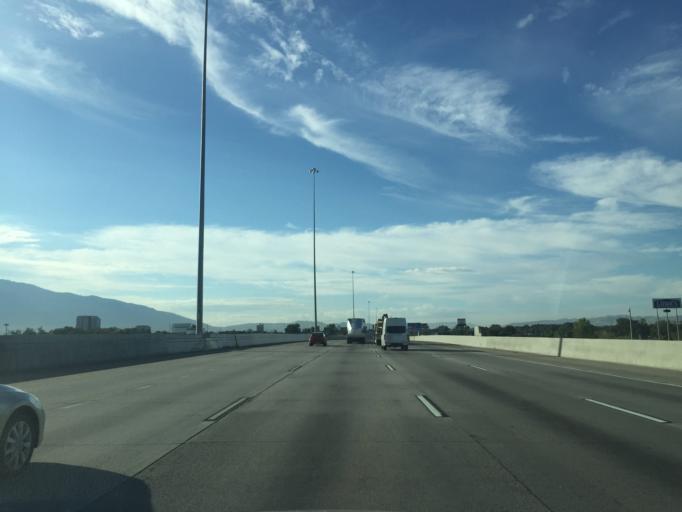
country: US
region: Utah
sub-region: Salt Lake County
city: Centerfield
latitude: 40.6755
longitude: -111.9018
